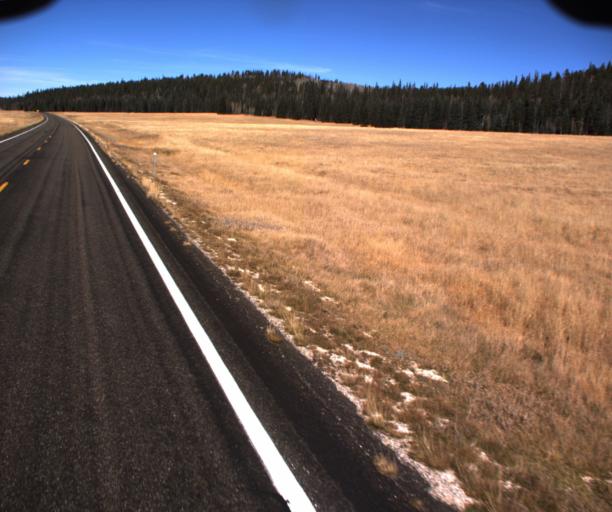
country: US
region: Arizona
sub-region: Coconino County
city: Grand Canyon
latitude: 36.3619
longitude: -112.1195
